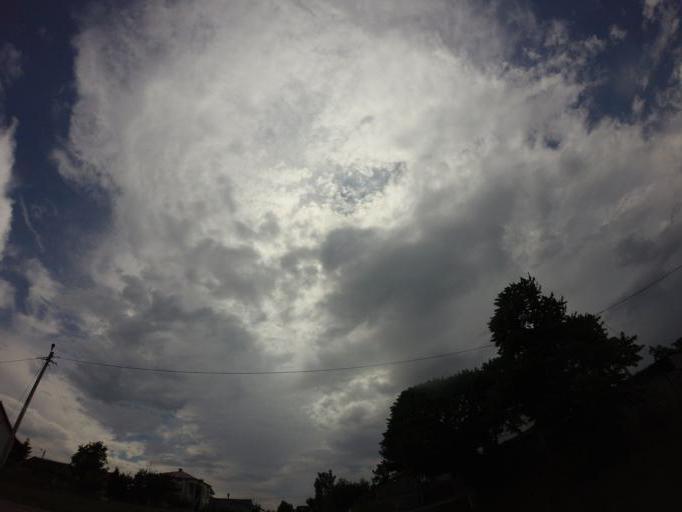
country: PL
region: Swietokrzyskie
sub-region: Powiat staszowski
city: Bogoria
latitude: 50.6327
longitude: 21.2380
